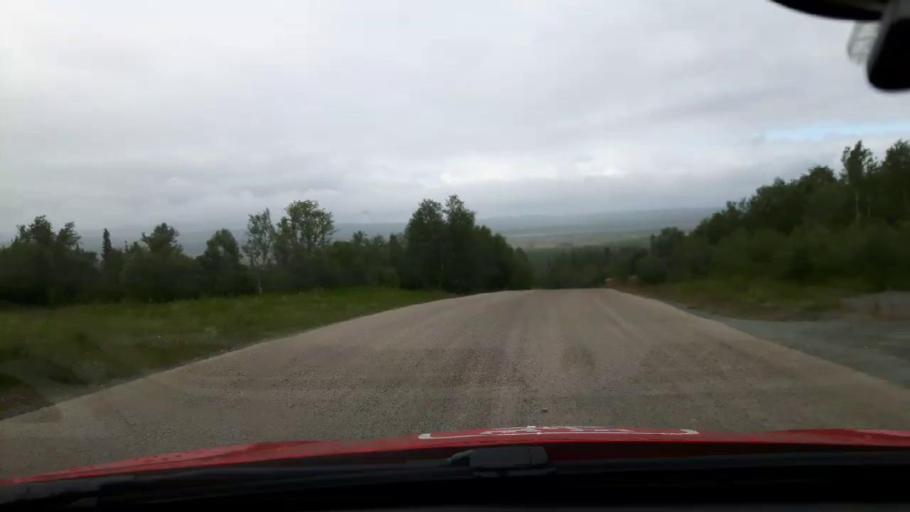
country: SE
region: Jaemtland
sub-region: Are Kommun
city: Are
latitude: 63.2537
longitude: 12.4267
